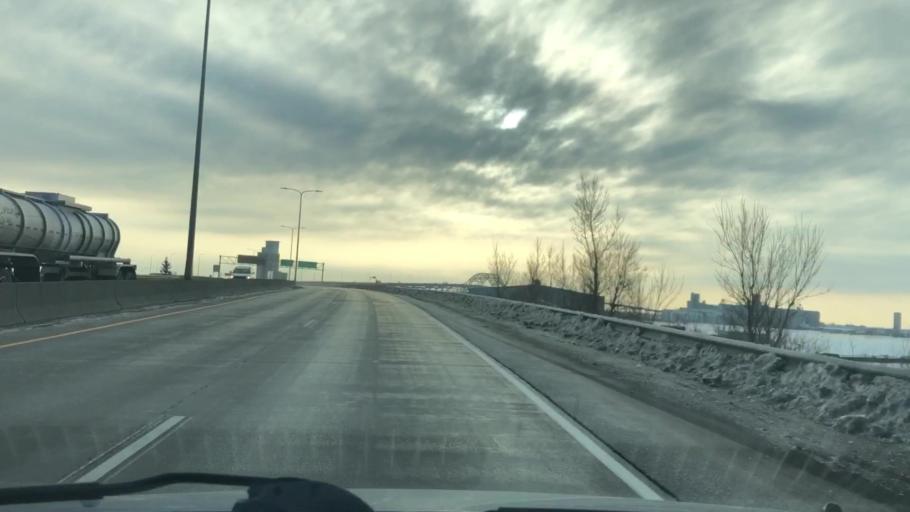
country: US
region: Minnesota
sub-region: Saint Louis County
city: Duluth
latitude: 46.7592
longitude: -92.1127
